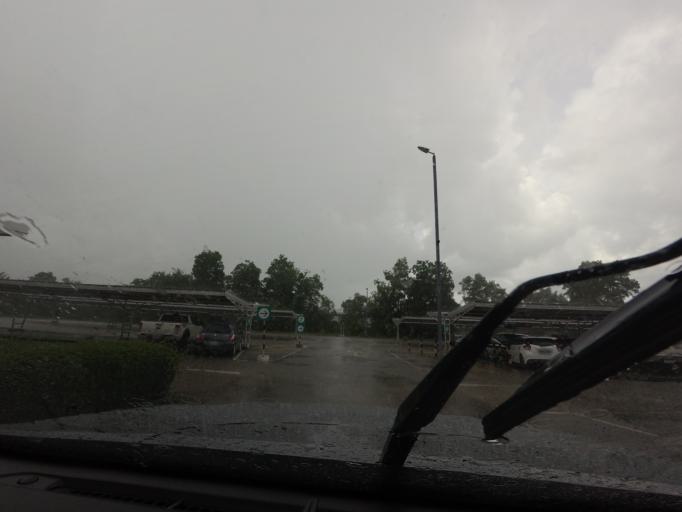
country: TH
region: Chumphon
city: Chumphon
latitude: 10.5041
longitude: 99.1394
